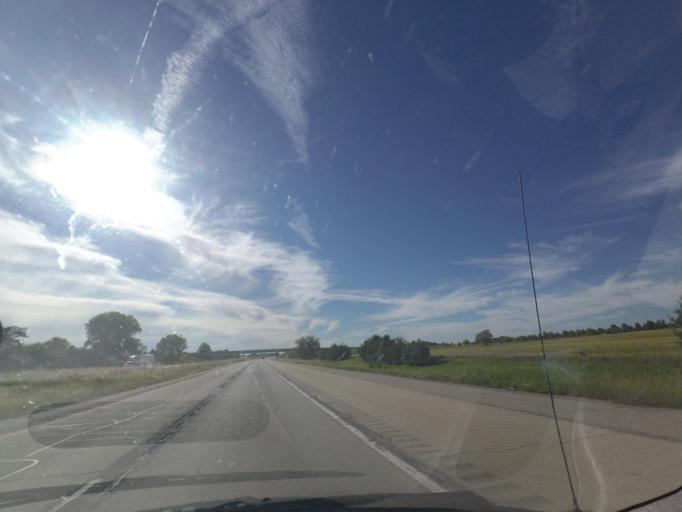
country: US
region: Illinois
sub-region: Macon County
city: Forsyth
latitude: 39.9079
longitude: -88.9708
